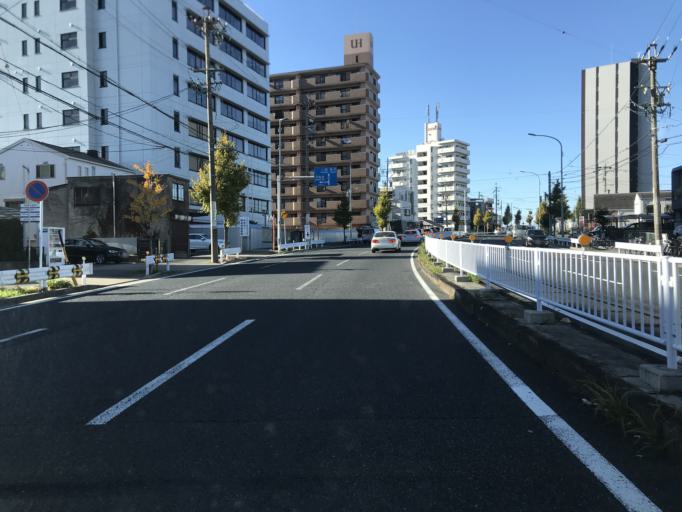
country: JP
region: Aichi
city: Nagoya-shi
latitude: 35.1895
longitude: 136.8696
